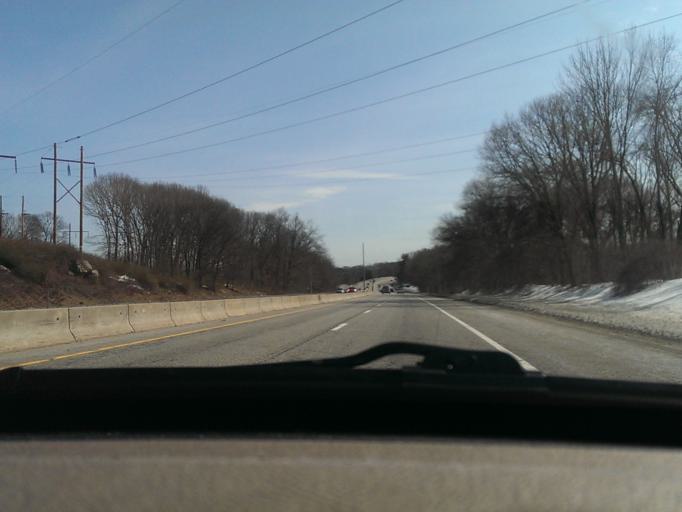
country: US
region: Rhode Island
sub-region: Providence County
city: North Providence
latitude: 41.8797
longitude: -71.4350
